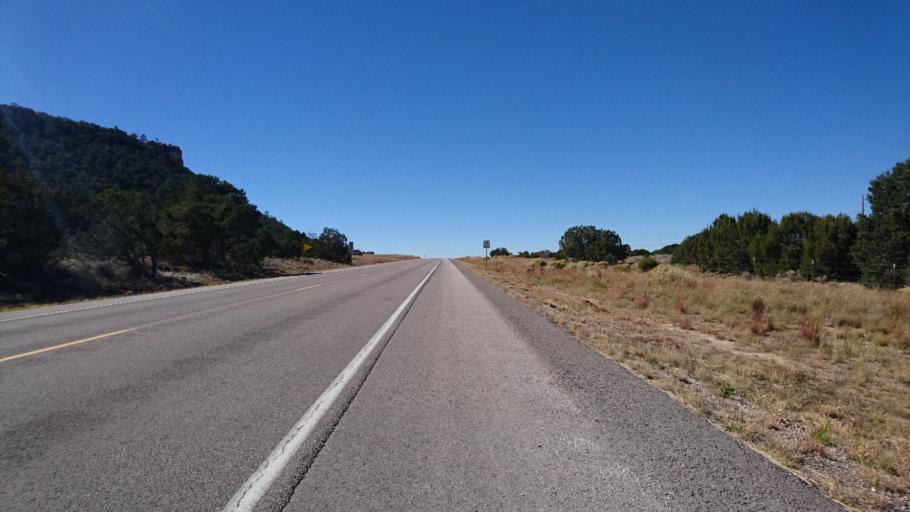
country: US
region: New Mexico
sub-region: McKinley County
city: Thoreau
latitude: 35.0449
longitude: -108.3063
